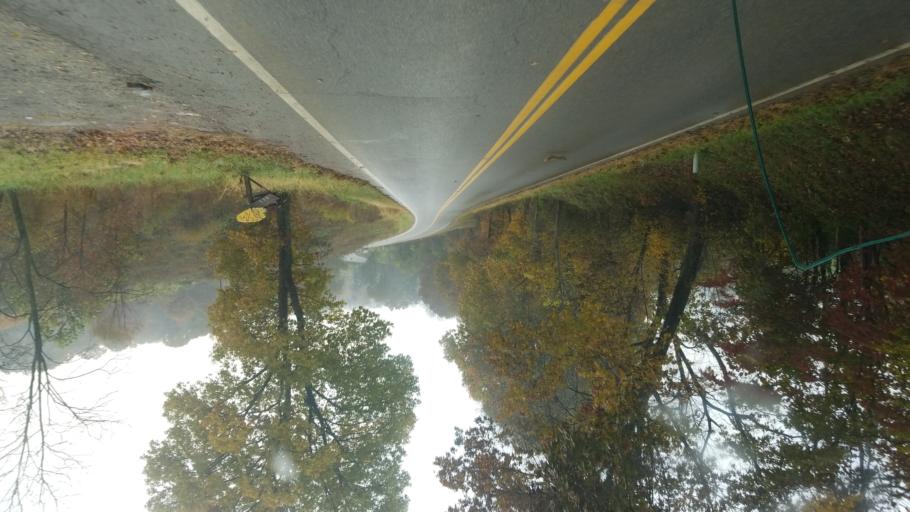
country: US
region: Ohio
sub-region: Morgan County
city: McConnelsville
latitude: 39.4734
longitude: -81.8822
